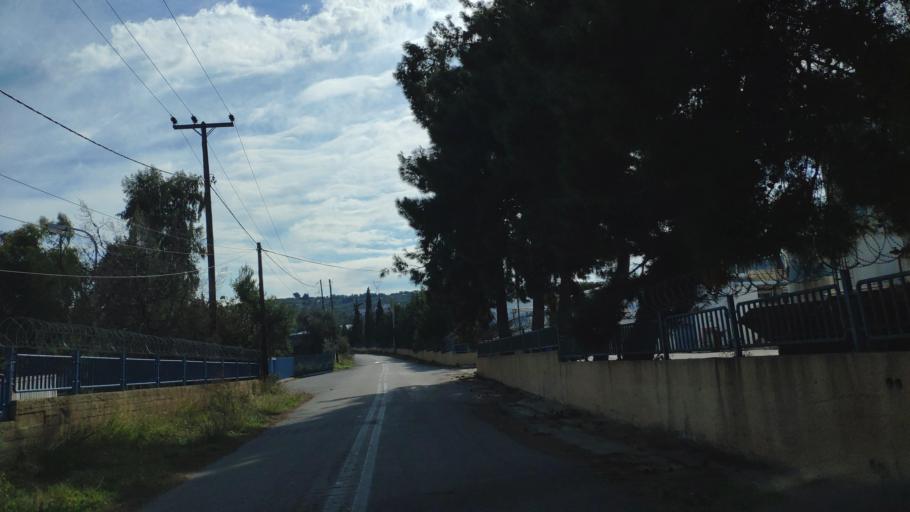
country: GR
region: Central Greece
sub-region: Nomos Evvoias
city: Vathi
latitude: 38.4186
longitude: 23.5913
